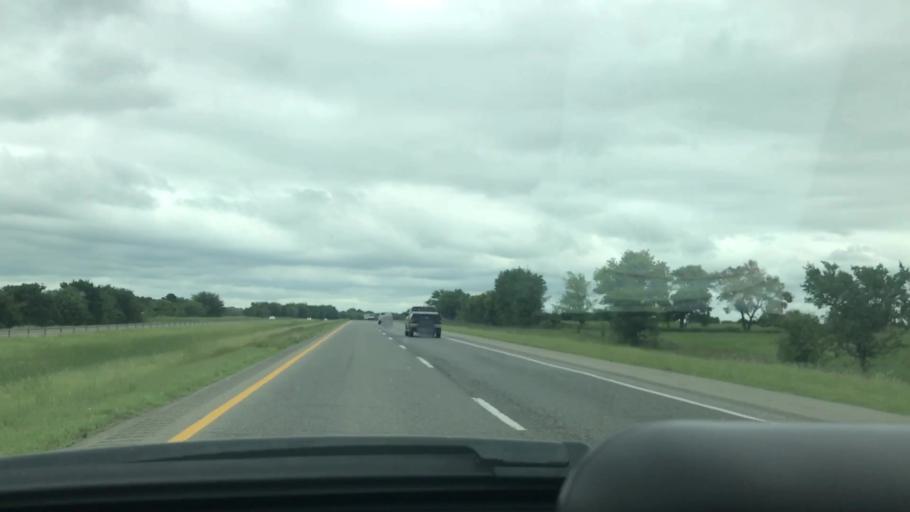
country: US
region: Oklahoma
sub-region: McIntosh County
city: Checotah
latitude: 35.4224
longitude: -95.5549
